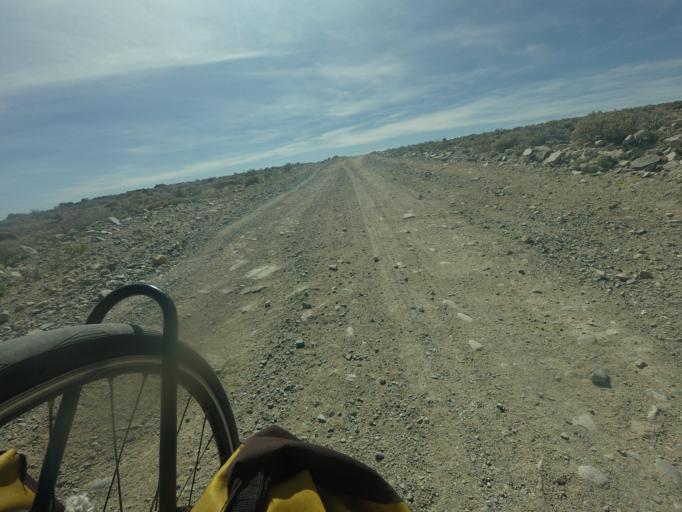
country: US
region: California
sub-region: San Bernardino County
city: Searles Valley
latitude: 35.6033
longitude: -117.3810
